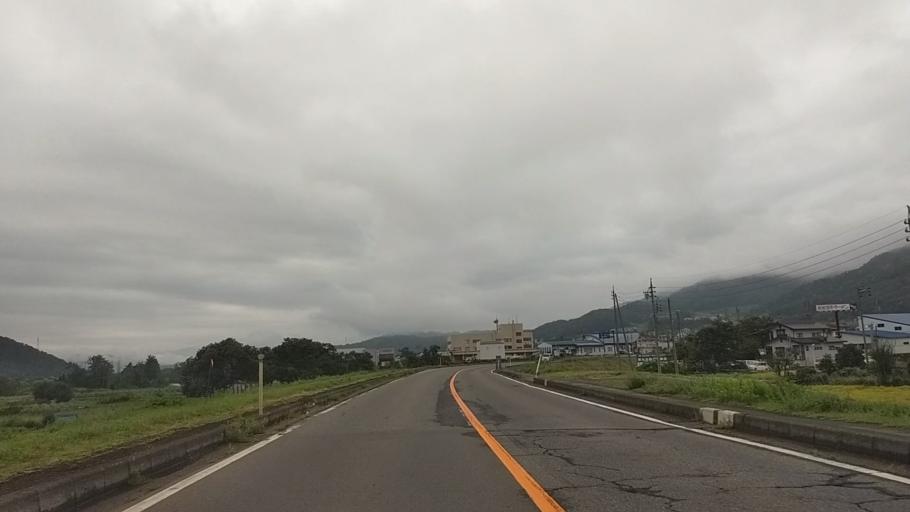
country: JP
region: Nagano
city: Iiyama
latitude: 36.8397
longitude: 138.3617
